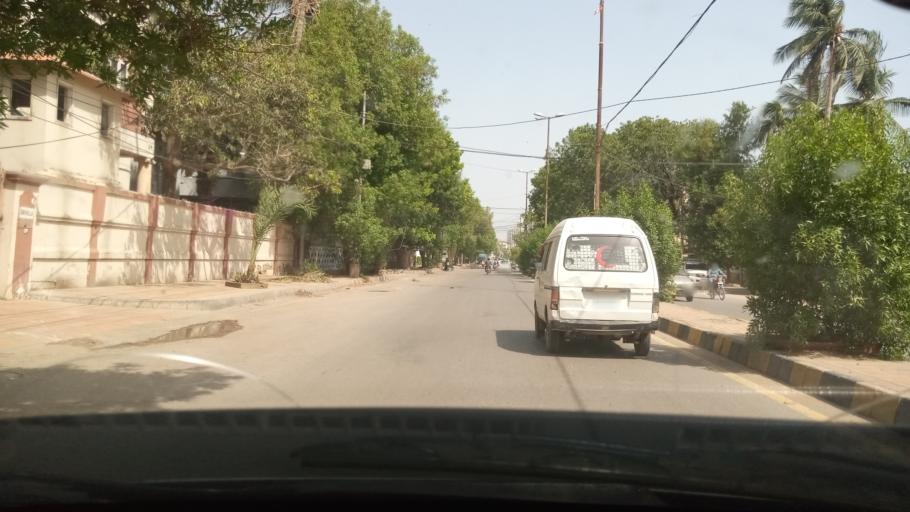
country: PK
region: Sindh
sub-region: Karachi District
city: Karachi
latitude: 24.8760
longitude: 67.0450
